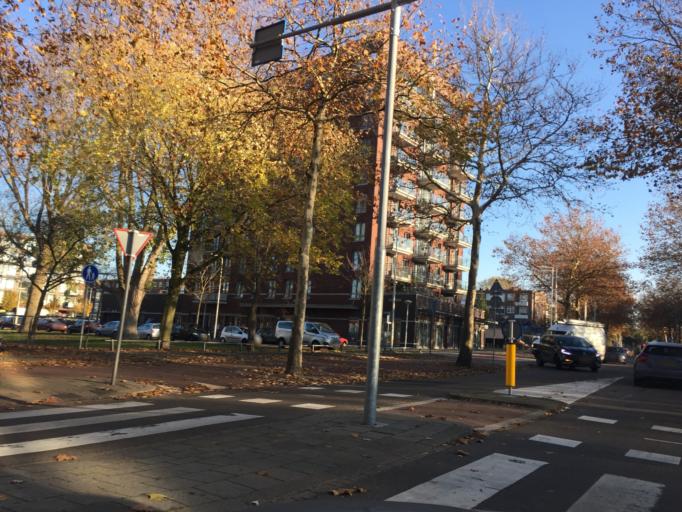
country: NL
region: South Holland
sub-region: Gemeente Westland
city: Kwintsheul
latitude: 52.0352
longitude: 4.2639
